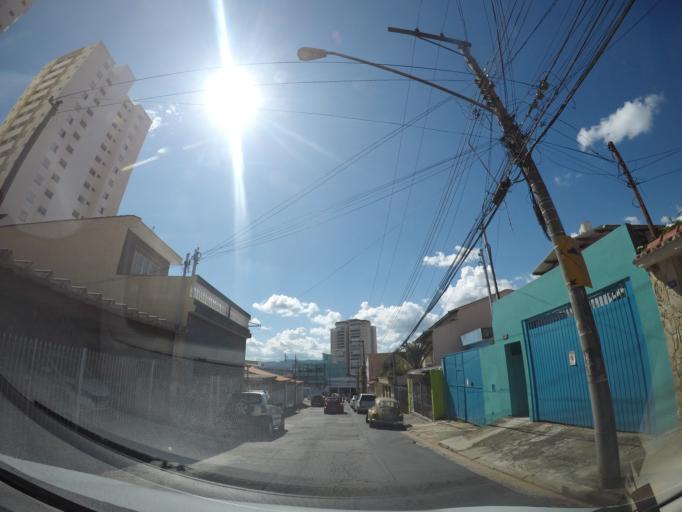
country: BR
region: Sao Paulo
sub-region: Guarulhos
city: Guarulhos
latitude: -23.4524
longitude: -46.5511
